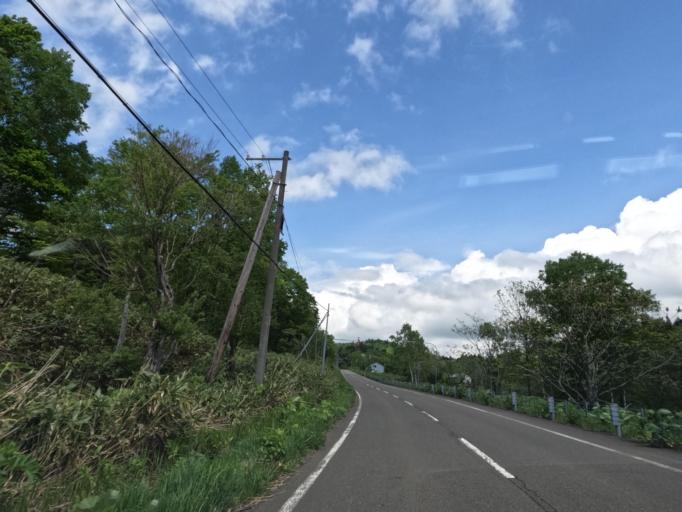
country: JP
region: Hokkaido
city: Takikawa
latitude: 43.5340
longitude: 141.5964
